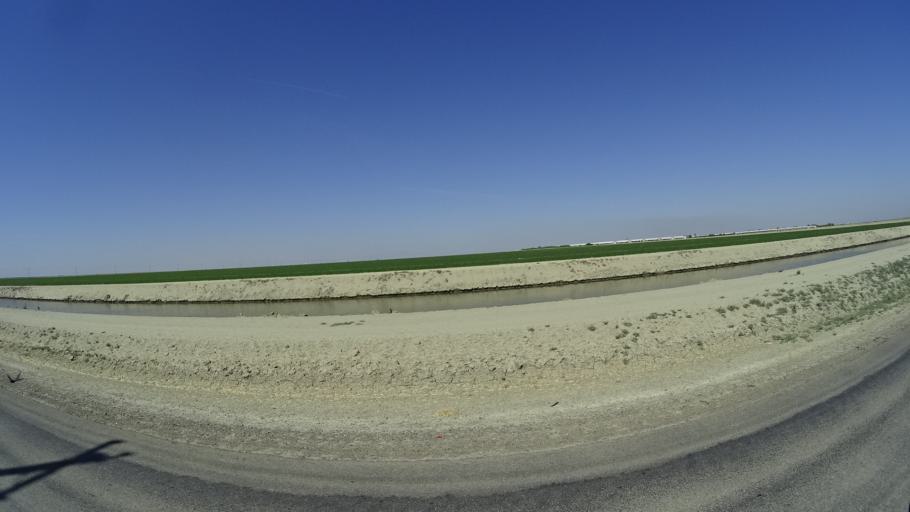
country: US
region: California
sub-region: Kings County
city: Corcoran
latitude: 35.9975
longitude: -119.5363
